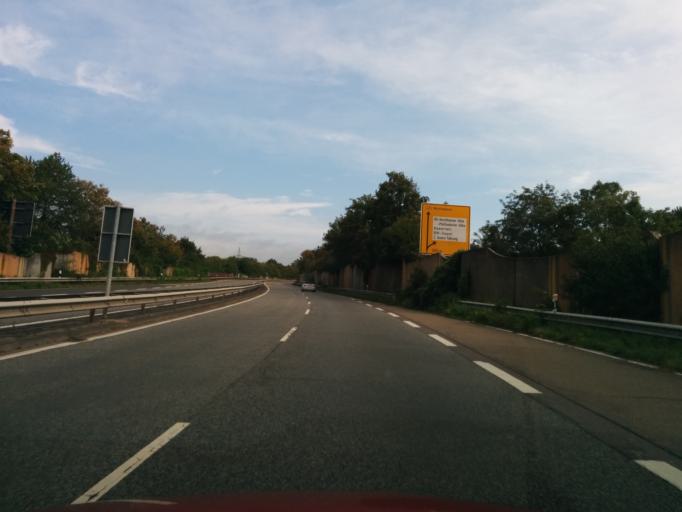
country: DE
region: Rheinland-Pfalz
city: Lahnstein
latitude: 50.3299
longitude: 7.6077
